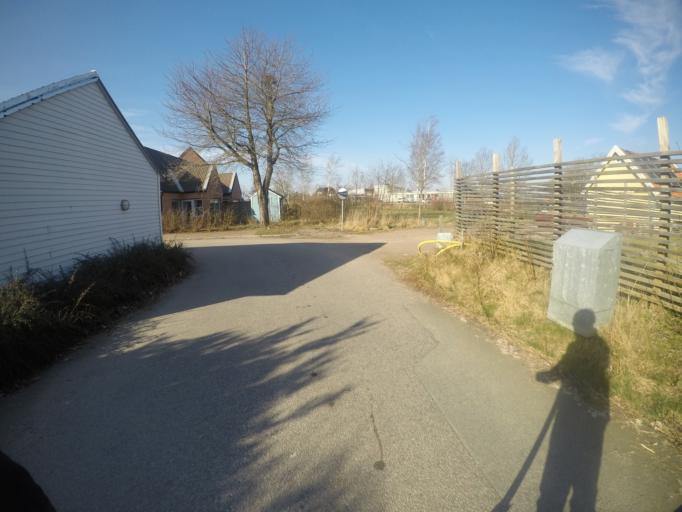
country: SE
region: Halland
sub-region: Laholms Kommun
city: Laholm
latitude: 56.5038
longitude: 13.0609
